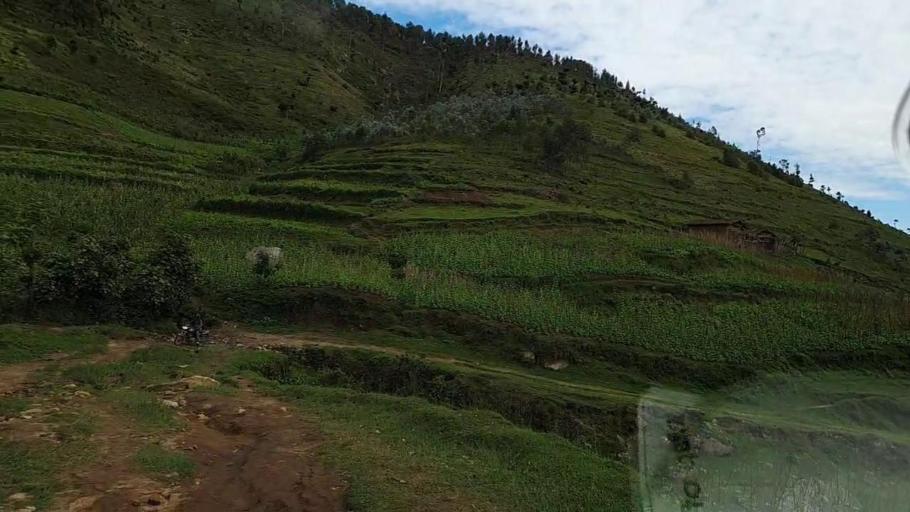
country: RW
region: Southern Province
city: Nzega
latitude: -2.4047
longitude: 29.4997
